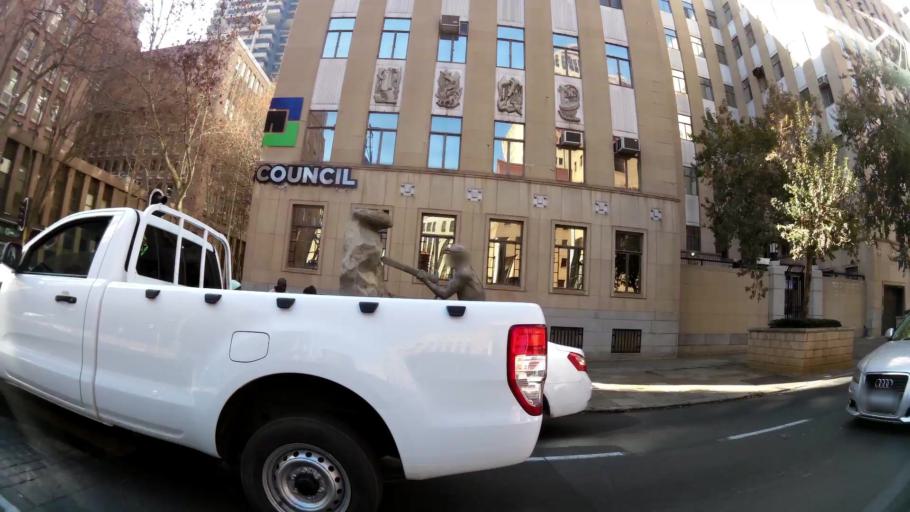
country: ZA
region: Gauteng
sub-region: City of Johannesburg Metropolitan Municipality
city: Johannesburg
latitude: -26.2073
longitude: 28.0384
